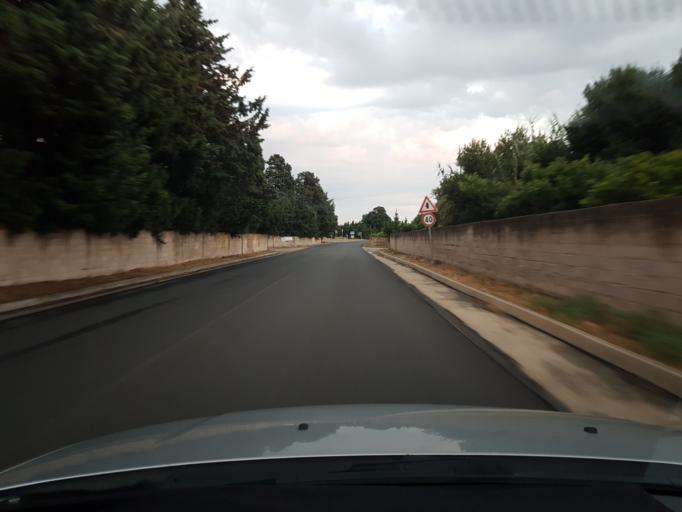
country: IT
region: Sardinia
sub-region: Provincia di Oristano
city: Milis
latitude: 40.0453
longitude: 8.6326
